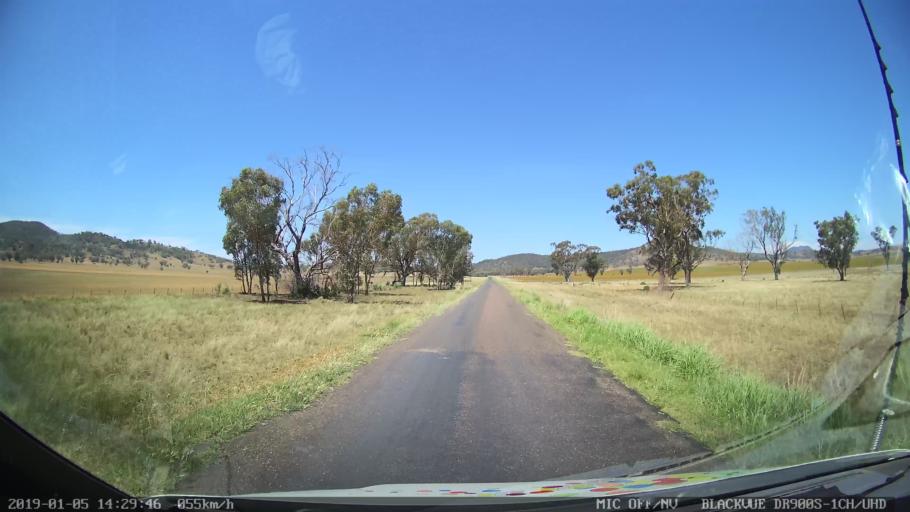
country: AU
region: New South Wales
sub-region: Tamworth Municipality
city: Phillip
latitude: -31.2282
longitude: 150.5844
